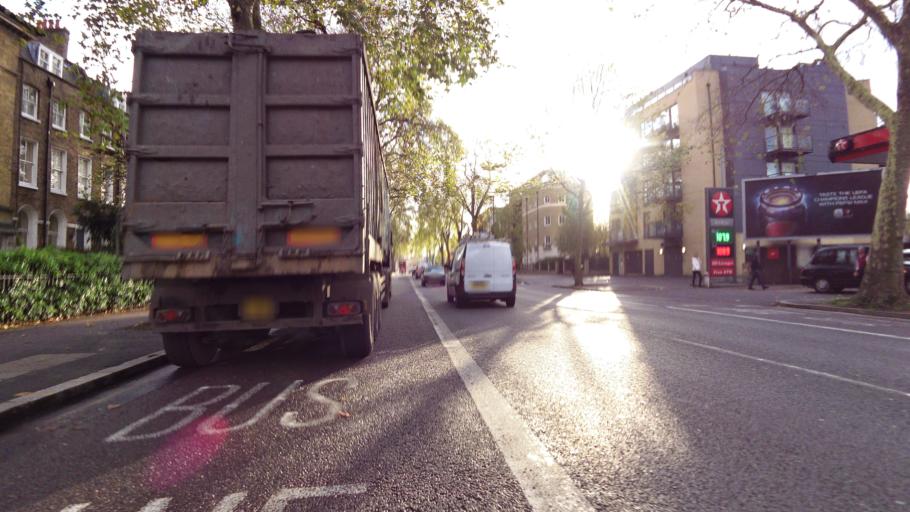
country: GB
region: England
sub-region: Greater London
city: Lambeth
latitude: 51.4909
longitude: -0.1110
